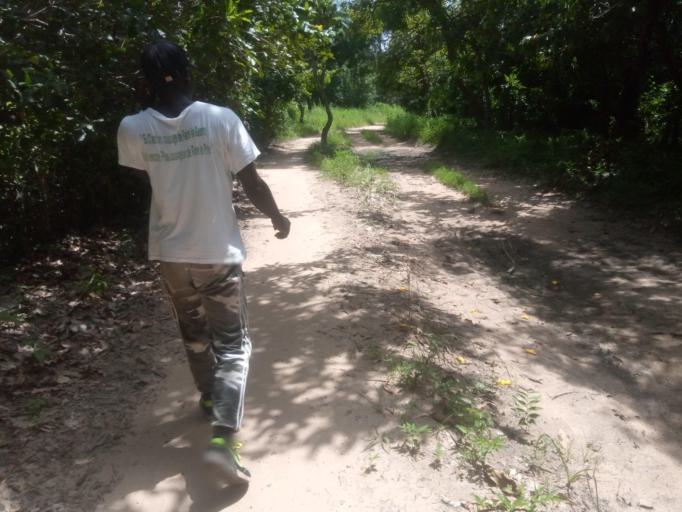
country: GM
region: Western
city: Gunjur
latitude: 13.0390
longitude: -16.7288
